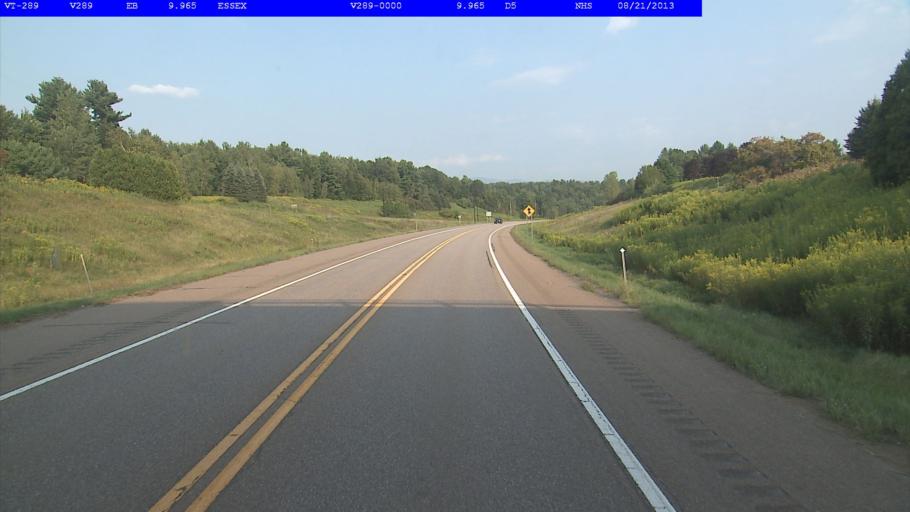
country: US
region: Vermont
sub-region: Chittenden County
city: Essex Junction
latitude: 44.5046
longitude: -73.0789
